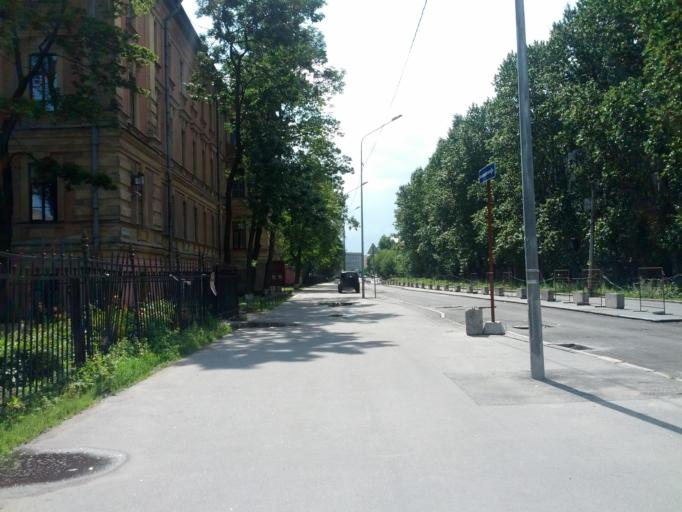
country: RU
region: St.-Petersburg
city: Admiralteisky
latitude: 59.8945
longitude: 30.3241
